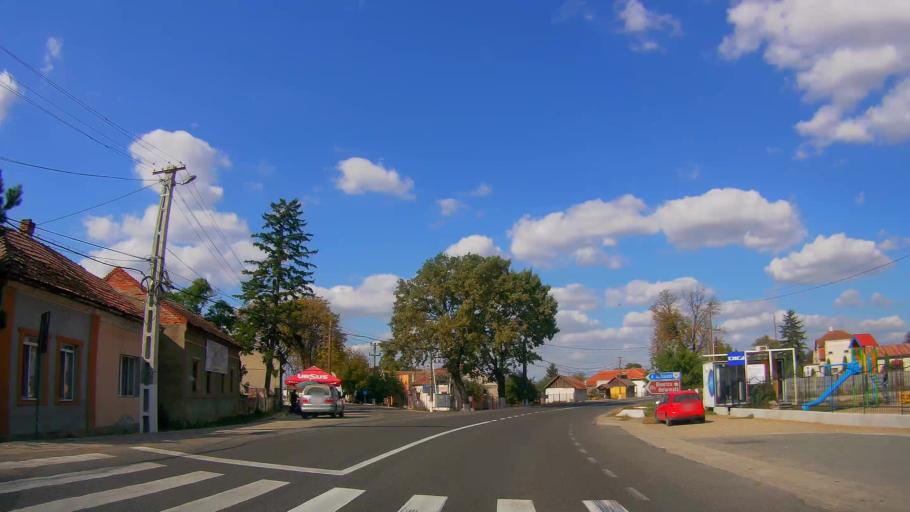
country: RO
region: Satu Mare
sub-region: Comuna Acas
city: Acas
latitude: 47.5381
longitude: 22.7835
